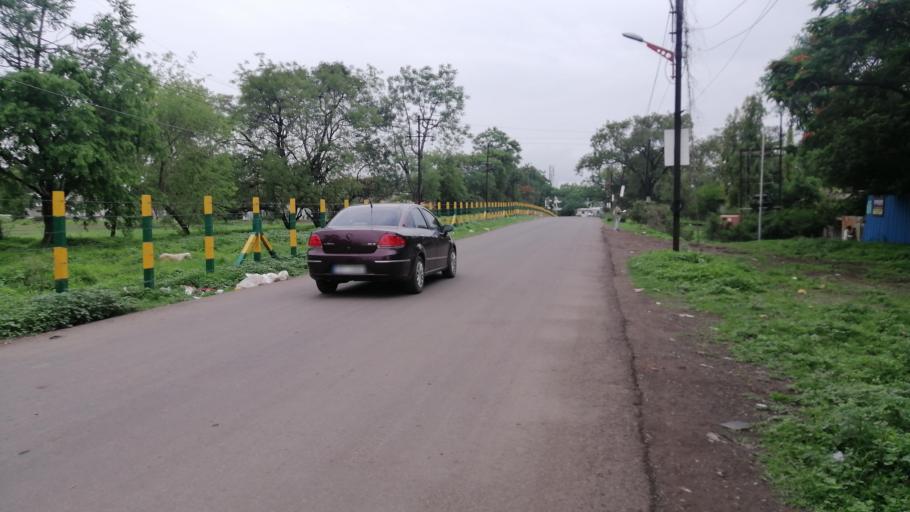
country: IN
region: Maharashtra
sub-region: Aurangabad Division
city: Aurangabad
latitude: 19.8765
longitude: 75.3768
